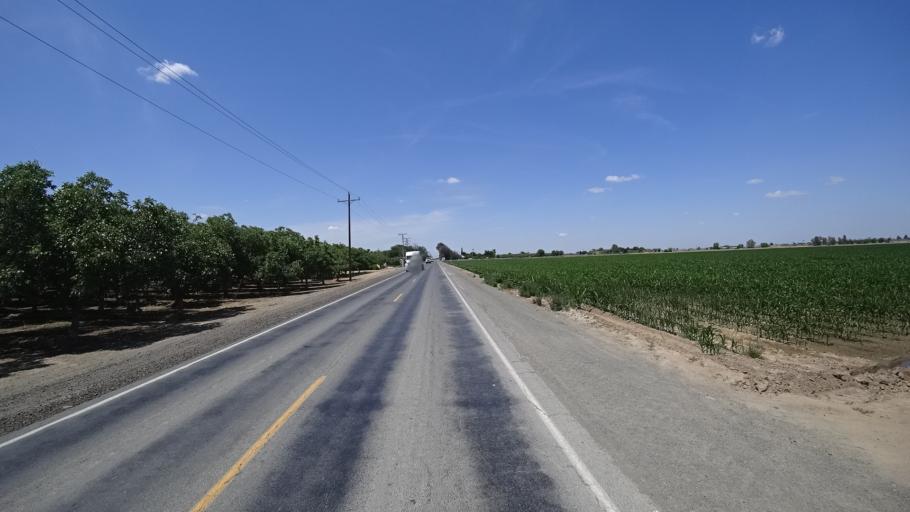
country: US
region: California
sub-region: Kings County
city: Home Garden
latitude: 36.2983
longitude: -119.6644
